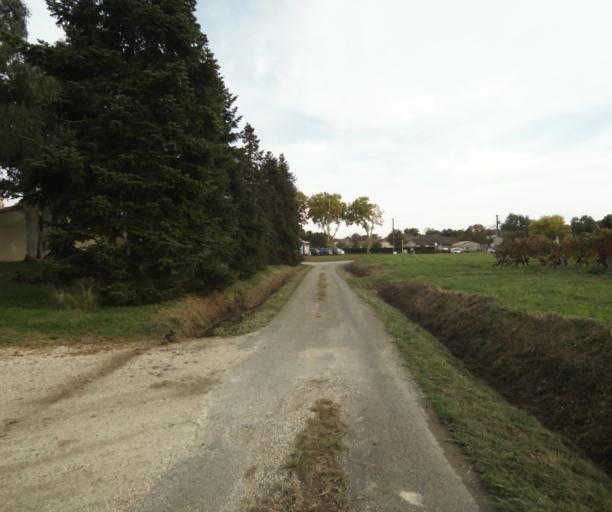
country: FR
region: Midi-Pyrenees
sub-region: Departement du Tarn-et-Garonne
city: Campsas
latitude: 43.8997
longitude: 1.3217
